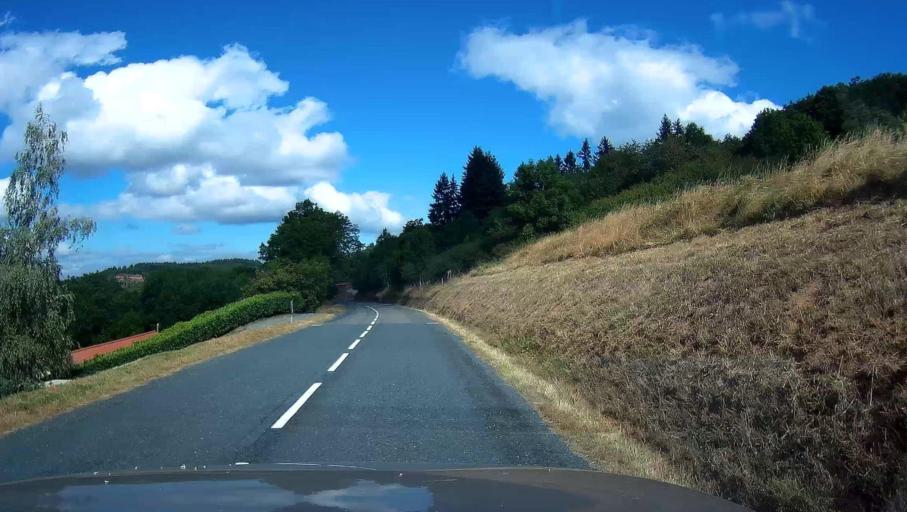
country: FR
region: Rhone-Alpes
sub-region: Departement du Rhone
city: Cogny
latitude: 45.9893
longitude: 4.5640
